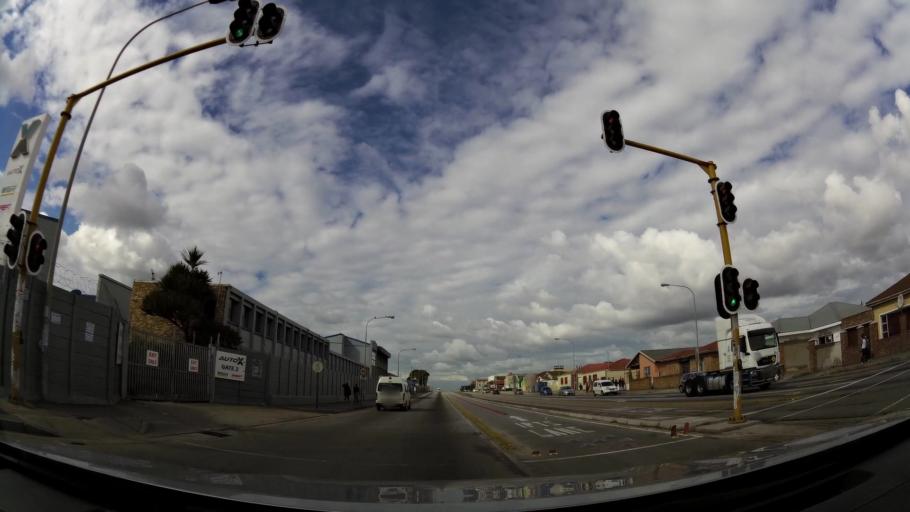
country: ZA
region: Eastern Cape
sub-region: Nelson Mandela Bay Metropolitan Municipality
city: Port Elizabeth
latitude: -33.9268
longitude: 25.5719
